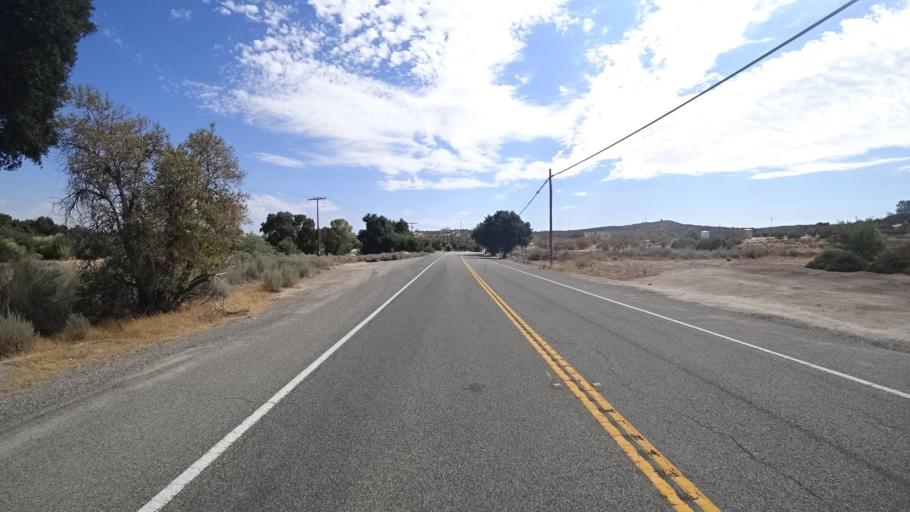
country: US
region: California
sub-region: San Diego County
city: Campo
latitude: 32.6722
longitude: -116.2903
